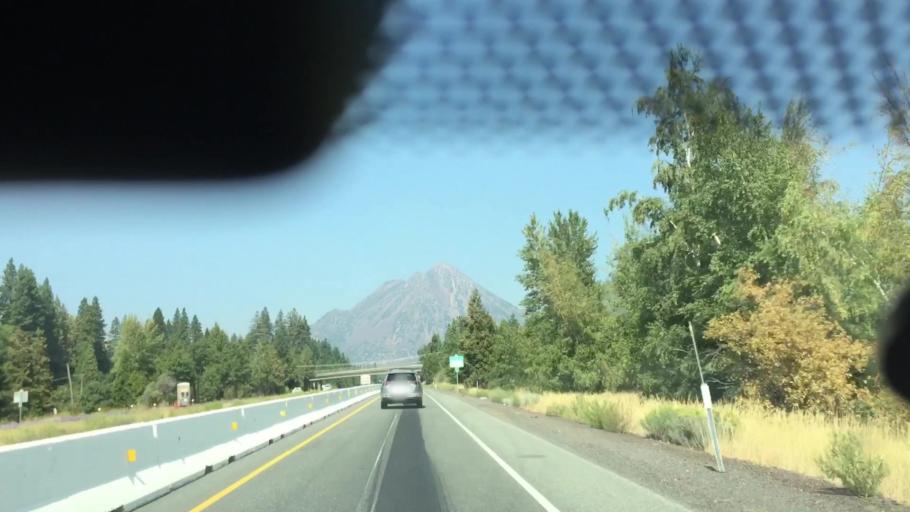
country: US
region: California
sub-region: Siskiyou County
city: Mount Shasta
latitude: 41.3162
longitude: -122.3233
